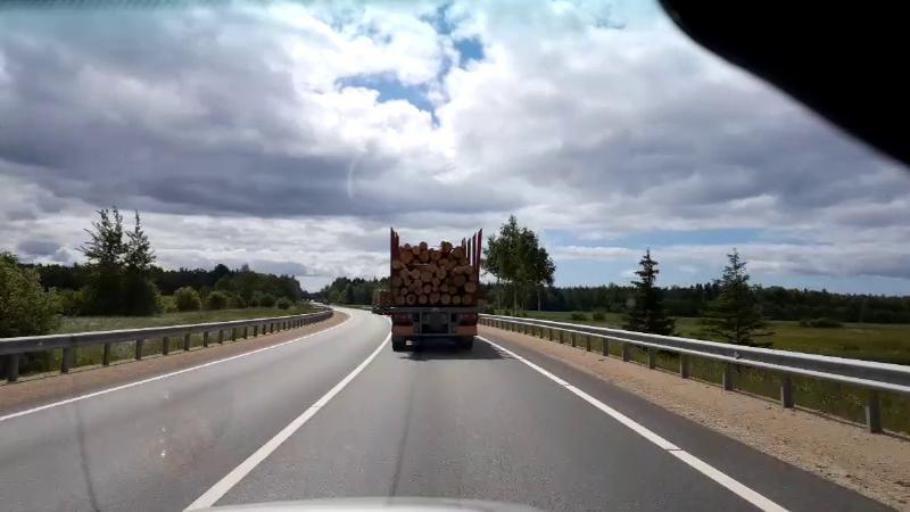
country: LV
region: Salacgrivas
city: Salacgriva
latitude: 57.7156
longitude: 24.3646
